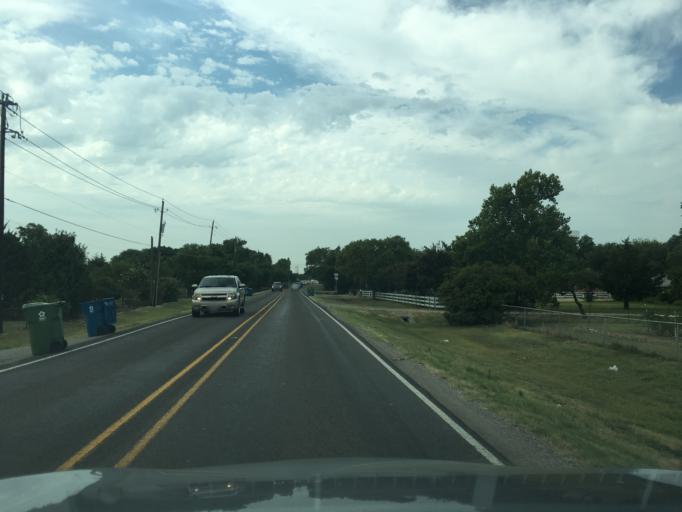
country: US
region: Texas
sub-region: Collin County
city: Parker
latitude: 33.0604
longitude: -96.6190
